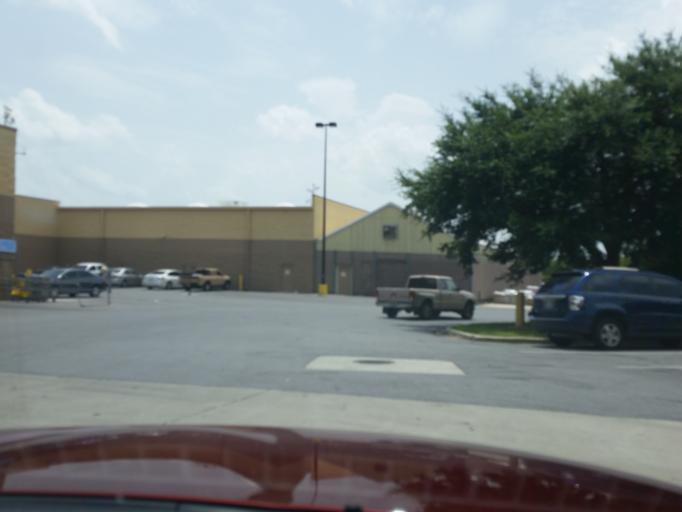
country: US
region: Florida
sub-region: Escambia County
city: Ensley
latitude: 30.5288
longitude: -87.2720
